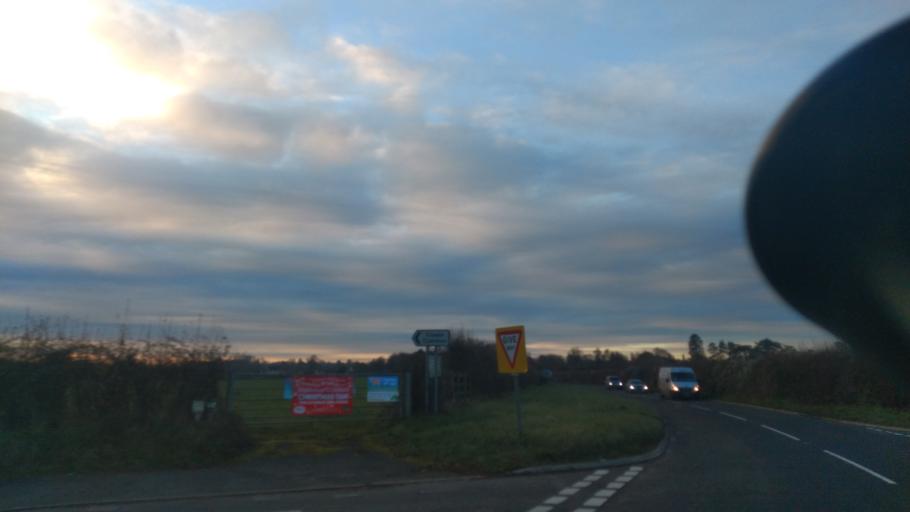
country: GB
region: England
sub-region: Wiltshire
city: Westwood
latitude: 51.3306
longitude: -2.2574
